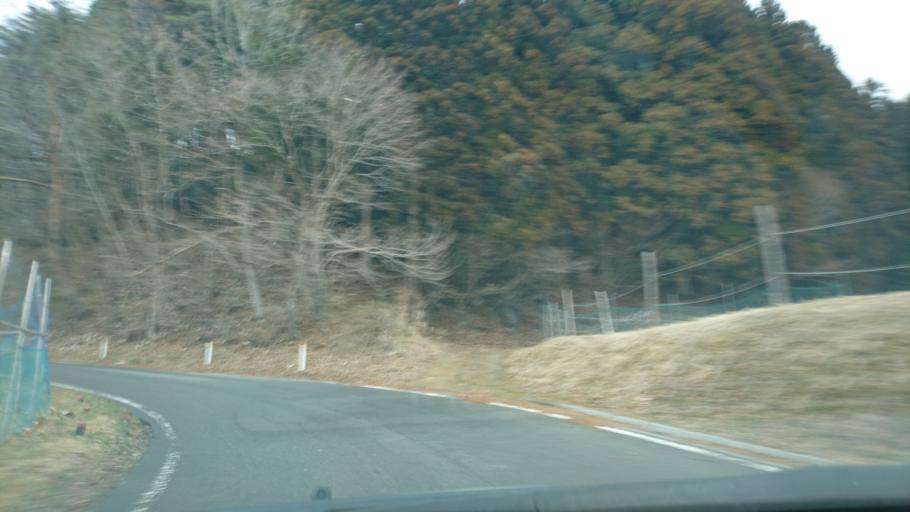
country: JP
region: Iwate
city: Ofunato
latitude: 38.9865
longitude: 141.5533
